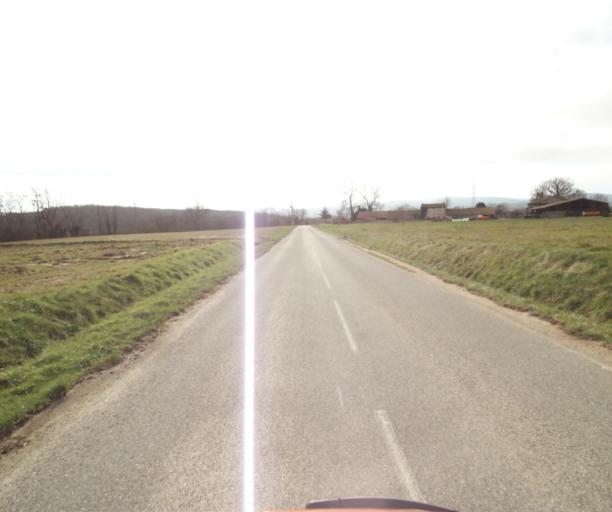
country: FR
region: Midi-Pyrenees
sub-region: Departement de l'Ariege
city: Pamiers
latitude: 43.1211
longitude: 1.5485
